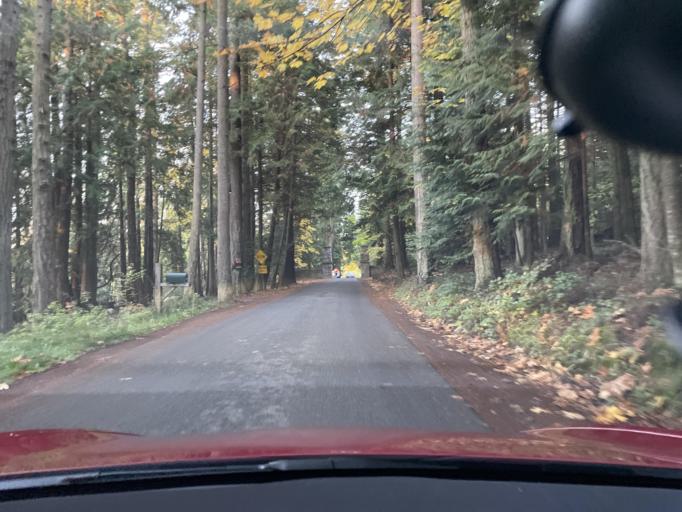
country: US
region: Washington
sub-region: San Juan County
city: Friday Harbor
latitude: 48.6156
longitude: -123.1527
